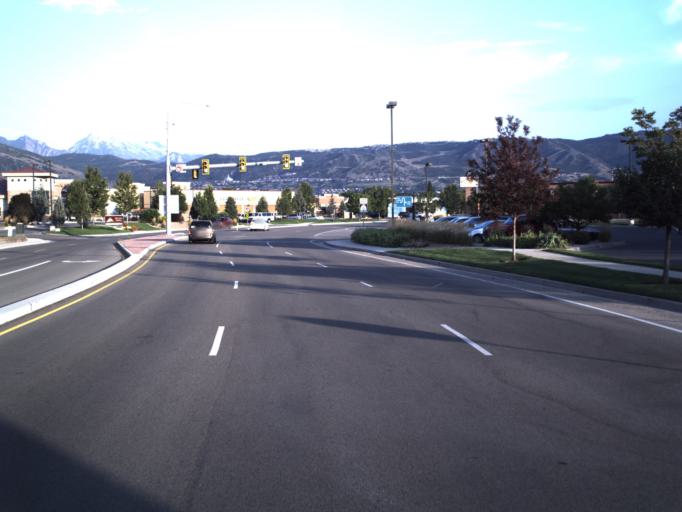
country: US
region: Utah
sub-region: Salt Lake County
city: Draper
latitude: 40.5290
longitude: -111.8901
